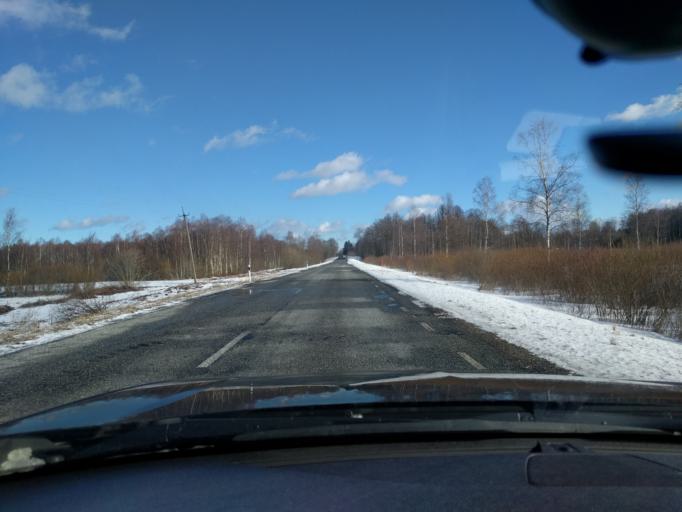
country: EE
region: Harju
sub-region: Raasiku vald
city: Raasiku
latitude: 59.4064
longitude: 25.2101
